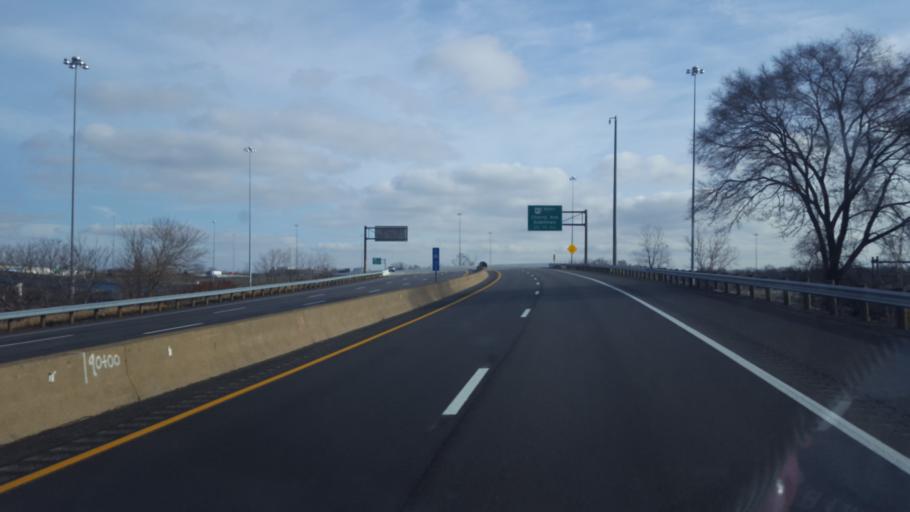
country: US
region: Ohio
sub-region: Stark County
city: Canton
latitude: 40.7843
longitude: -81.3880
